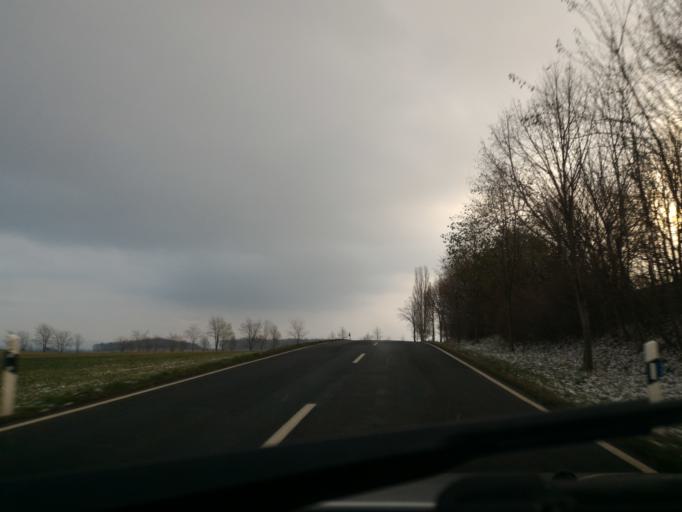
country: DE
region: Saxony
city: Hainewalde
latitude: 50.8998
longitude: 14.7089
